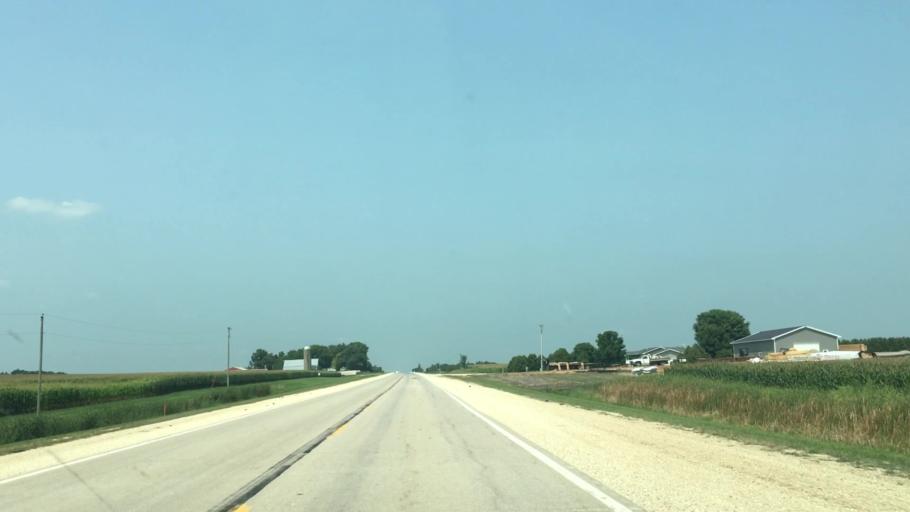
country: US
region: Iowa
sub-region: Fayette County
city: Fayette
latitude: 42.7652
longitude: -91.8045
